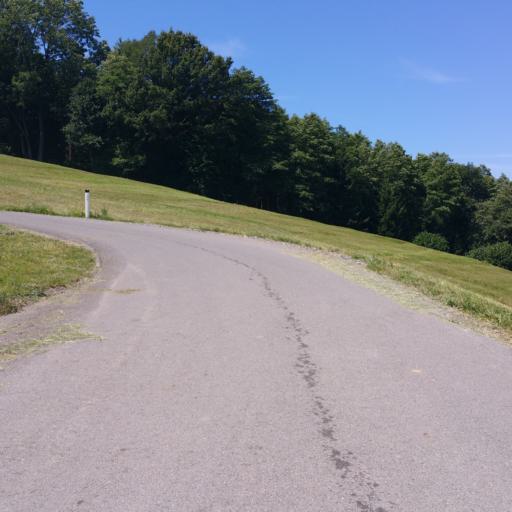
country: AT
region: Styria
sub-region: Politischer Bezirk Leibnitz
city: Gleinstatten
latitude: 46.7384
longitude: 15.3512
